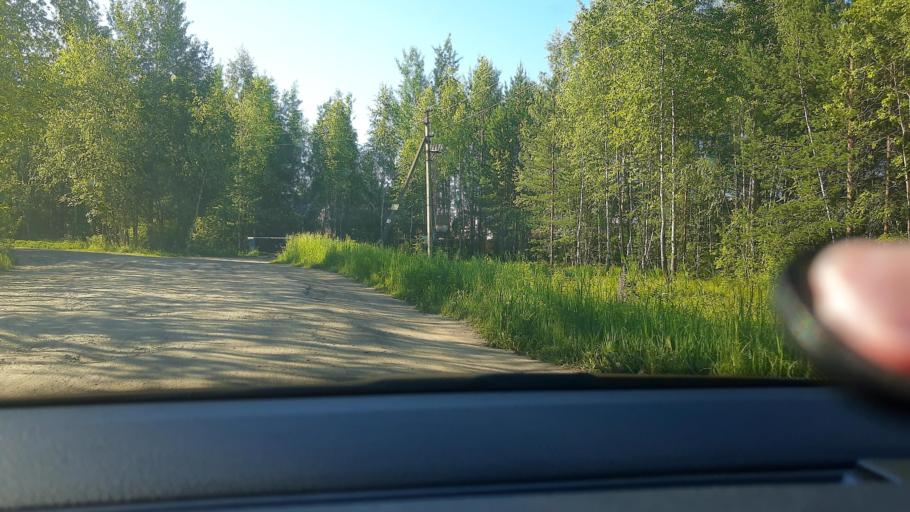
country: RU
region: Moskovskaya
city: Elektrogorsk
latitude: 55.8939
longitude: 38.7181
